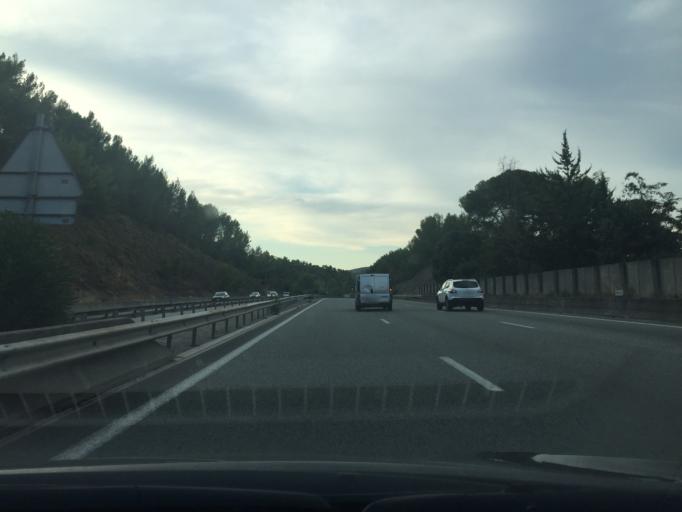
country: FR
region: Provence-Alpes-Cote d'Azur
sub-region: Departement du Var
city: Frejus
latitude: 43.4796
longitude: 6.7413
